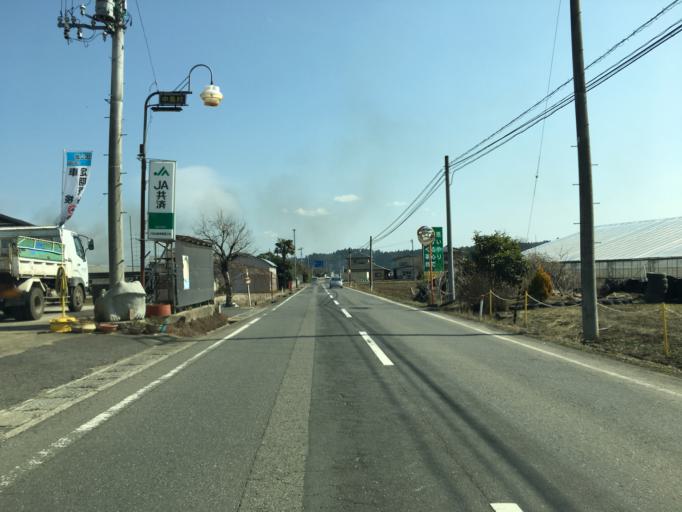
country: JP
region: Fukushima
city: Ishikawa
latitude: 37.1567
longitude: 140.3816
